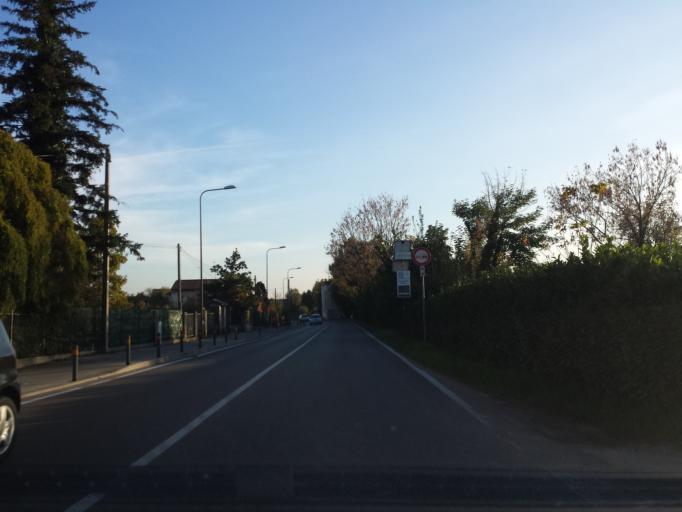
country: IT
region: Veneto
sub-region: Provincia di Vicenza
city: Crispi Cavour
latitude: 45.5789
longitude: 11.5349
